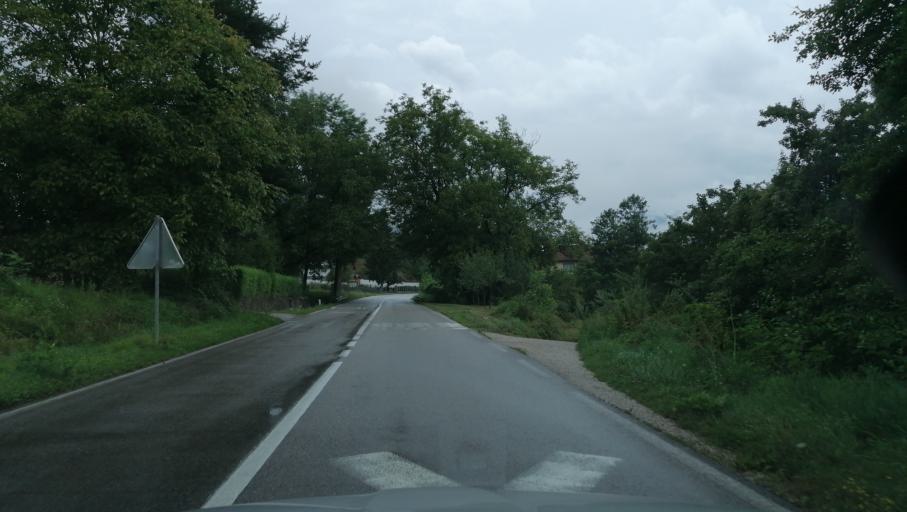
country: RS
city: Durici
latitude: 43.7578
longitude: 19.3867
